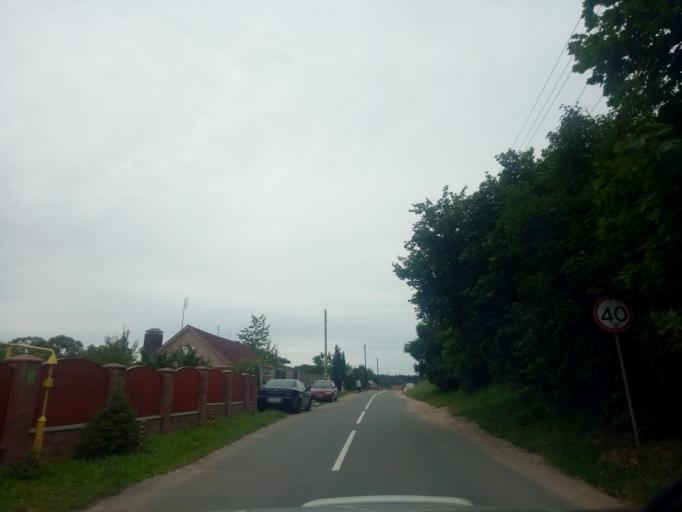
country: BY
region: Minsk
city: Zhdanovichy
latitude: 53.9269
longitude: 27.3838
